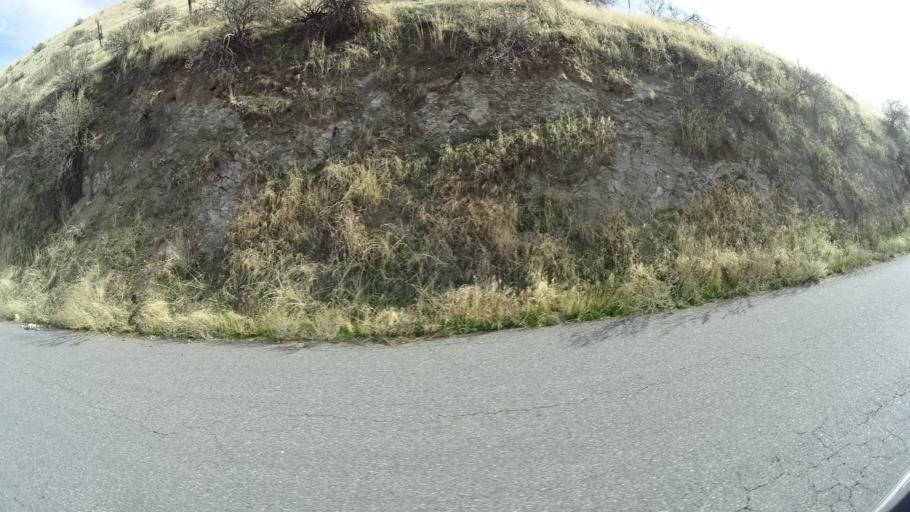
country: US
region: California
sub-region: Kern County
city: Bear Valley Springs
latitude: 35.2842
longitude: -118.6717
